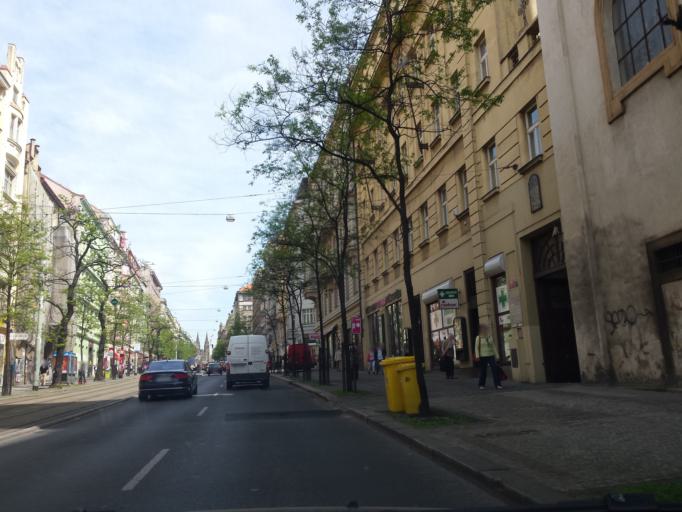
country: CZ
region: Praha
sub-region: Praha 2
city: Vysehrad
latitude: 50.0756
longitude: 14.4214
